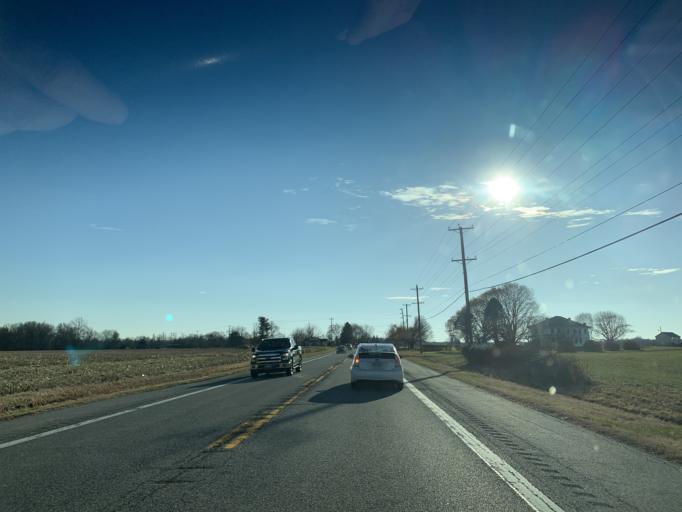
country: US
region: Maryland
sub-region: Cecil County
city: Elkton
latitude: 39.4919
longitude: -75.8437
